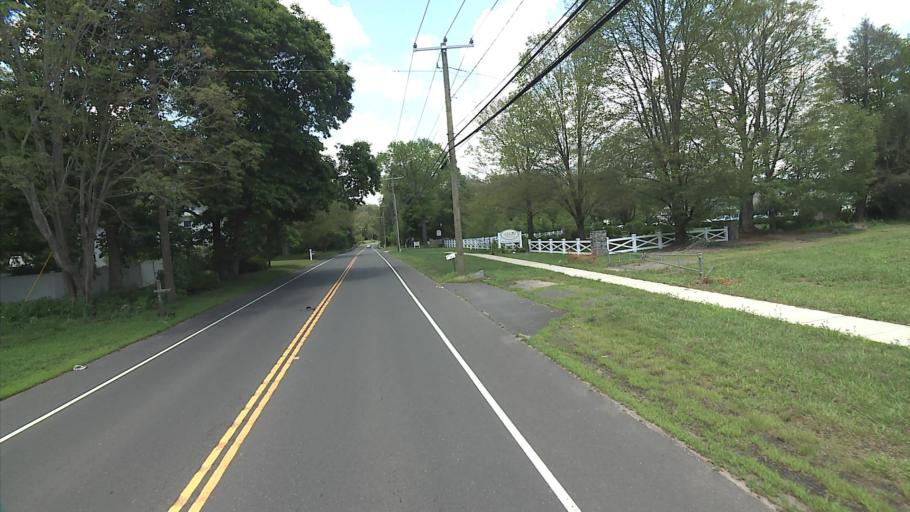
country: US
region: Connecticut
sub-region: Middlesex County
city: East Haddam
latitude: 41.4501
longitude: -72.4773
